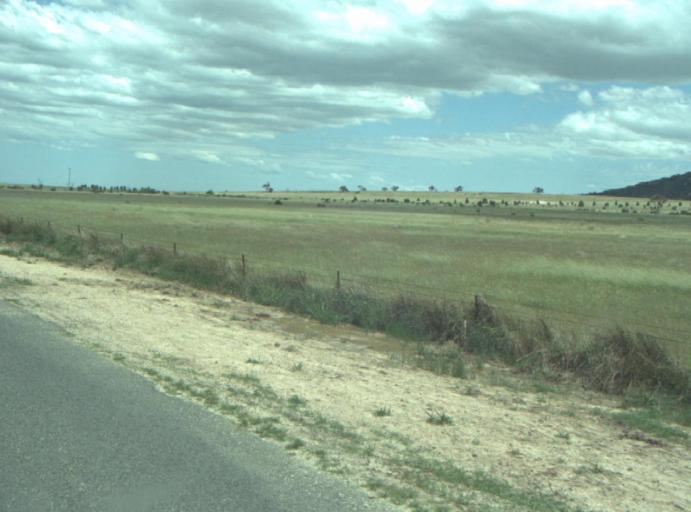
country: AU
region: Victoria
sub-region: Wyndham
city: Little River
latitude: -37.9283
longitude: 144.4647
